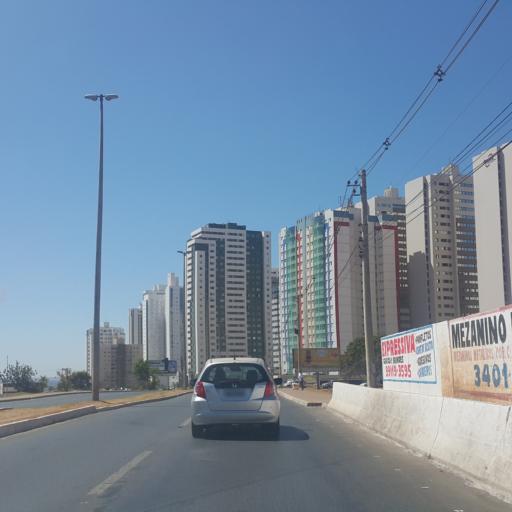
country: BR
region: Federal District
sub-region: Brasilia
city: Brasilia
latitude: -15.8369
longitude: -48.0433
